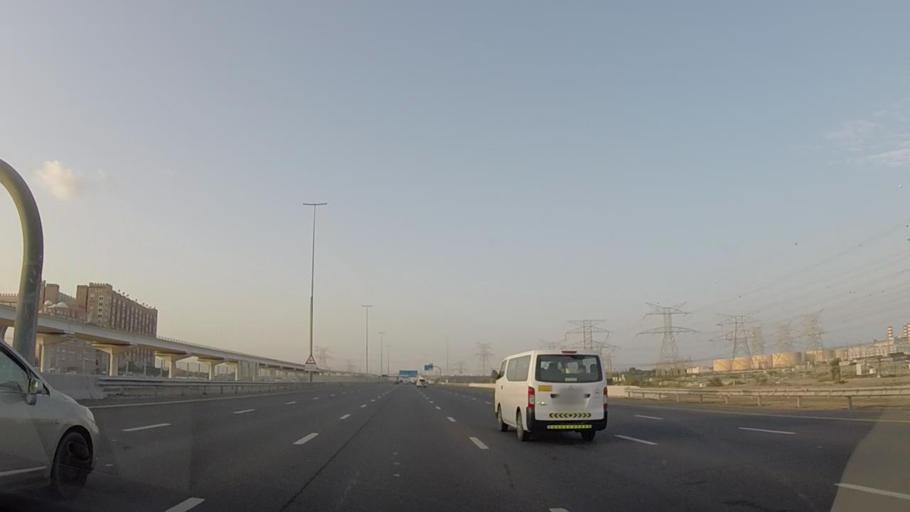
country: AE
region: Dubai
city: Dubai
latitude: 25.0458
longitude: 55.1157
